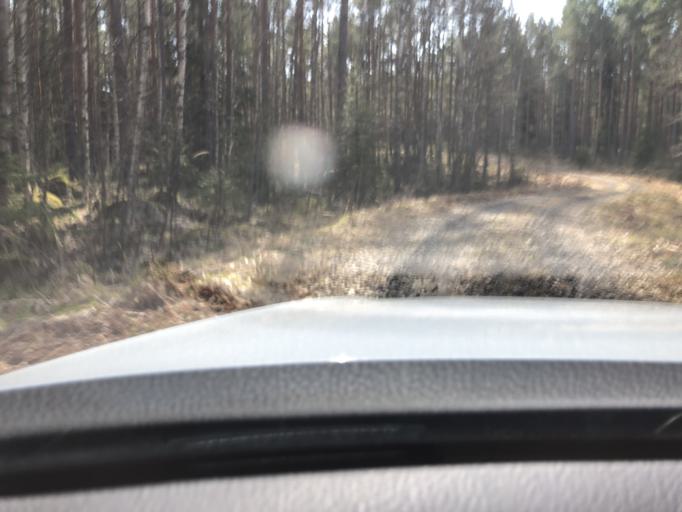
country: SE
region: Uppsala
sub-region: Heby Kommun
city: OEstervala
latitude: 60.3332
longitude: 17.1717
